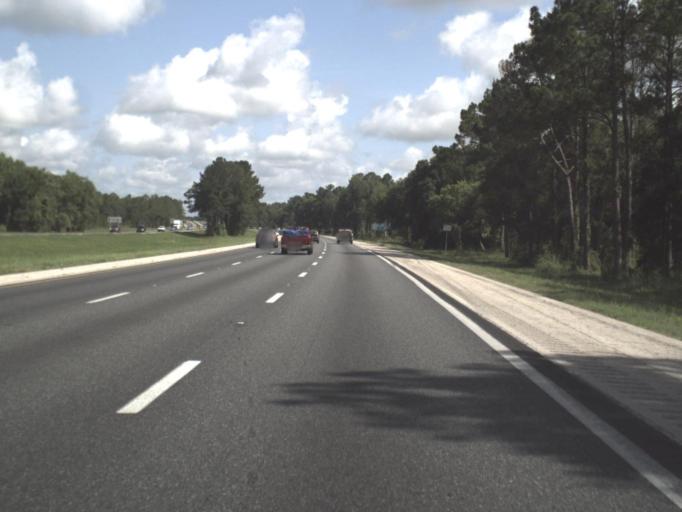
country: US
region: Florida
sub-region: Alachua County
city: Gainesville
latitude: 29.5086
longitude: -82.2998
